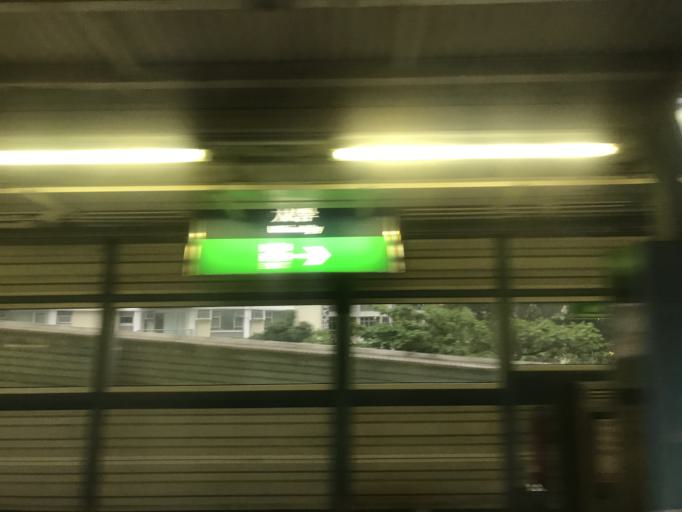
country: HK
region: Sha Tin
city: Sha Tin
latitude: 22.4132
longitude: 114.2099
